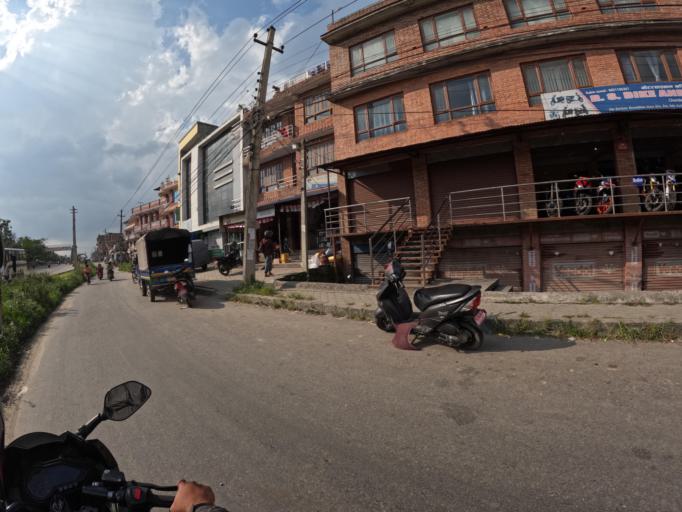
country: NP
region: Central Region
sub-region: Bagmati Zone
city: Bhaktapur
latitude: 27.6669
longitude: 85.4178
